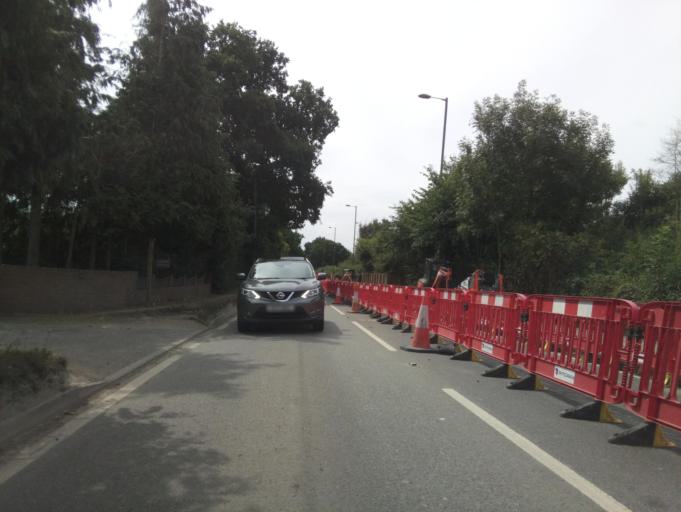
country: GB
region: England
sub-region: Surrey
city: Salfords
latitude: 51.1854
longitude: -0.1957
